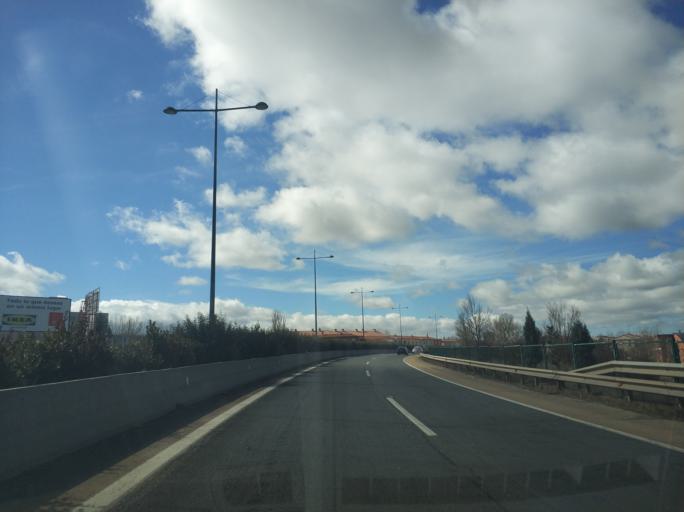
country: ES
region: Castille and Leon
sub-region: Provincia de Burgos
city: Burgos
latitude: 42.3379
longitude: -3.6852
